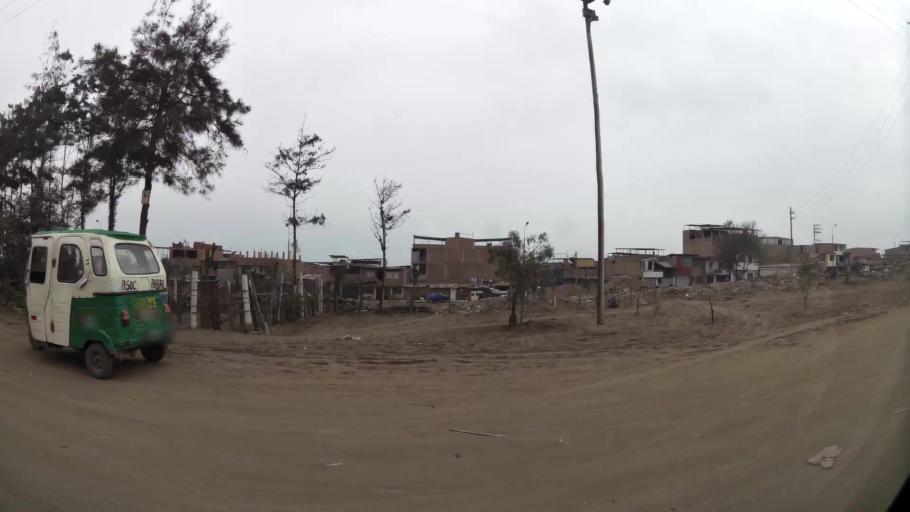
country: PE
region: Lima
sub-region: Lima
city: Surco
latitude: -12.2165
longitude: -76.9269
